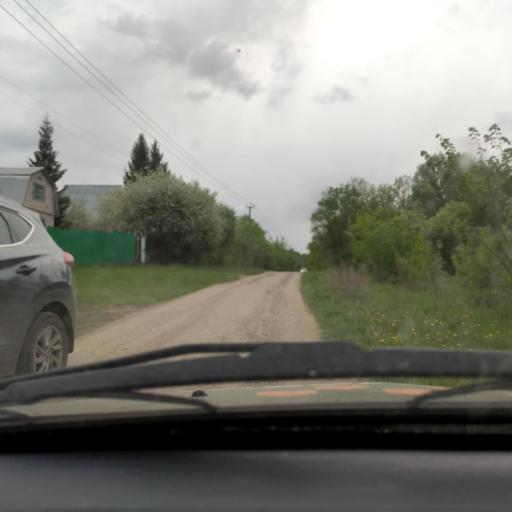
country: RU
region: Bashkortostan
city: Avdon
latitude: 54.5945
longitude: 55.6877
